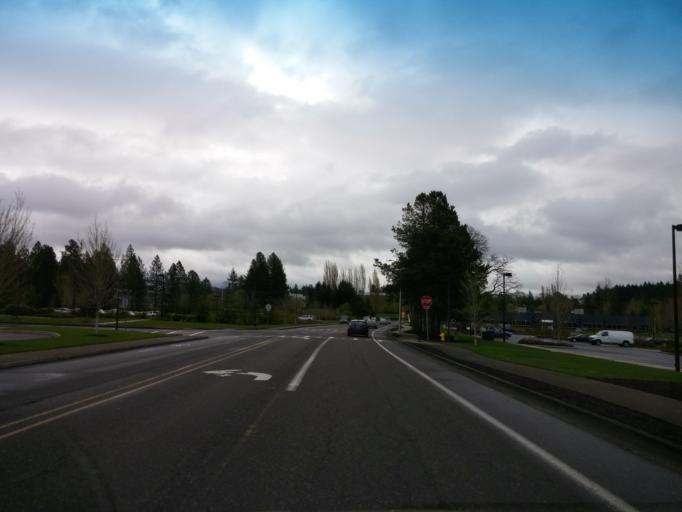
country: US
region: Oregon
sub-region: Washington County
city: Cedar Mill
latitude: 45.5095
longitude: -122.8378
